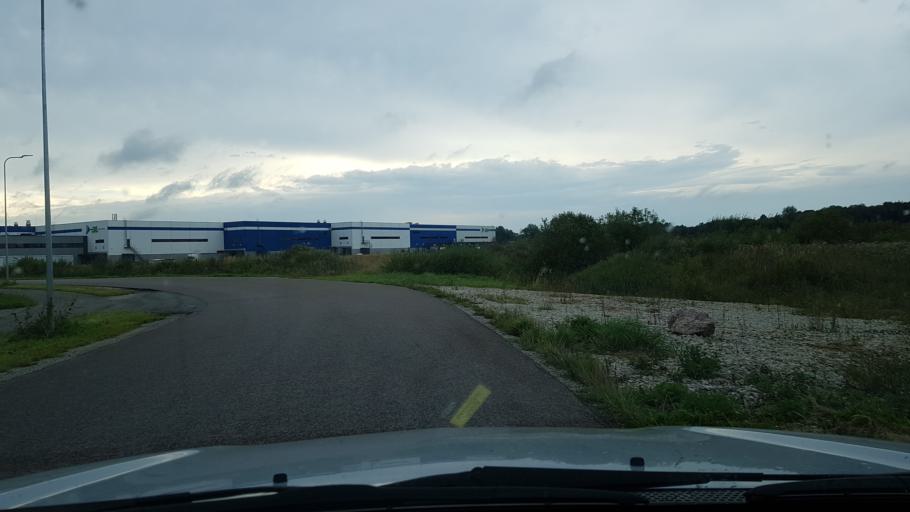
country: EE
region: Harju
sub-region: Joelaehtme vald
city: Loo
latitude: 59.3977
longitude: 24.9250
